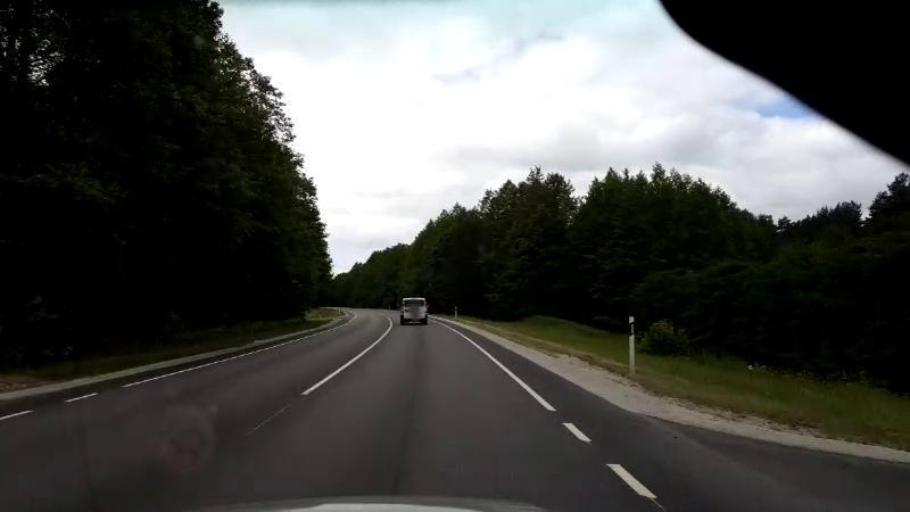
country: EE
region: Paernumaa
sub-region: Paernu linn
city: Parnu
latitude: 58.2220
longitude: 24.4903
